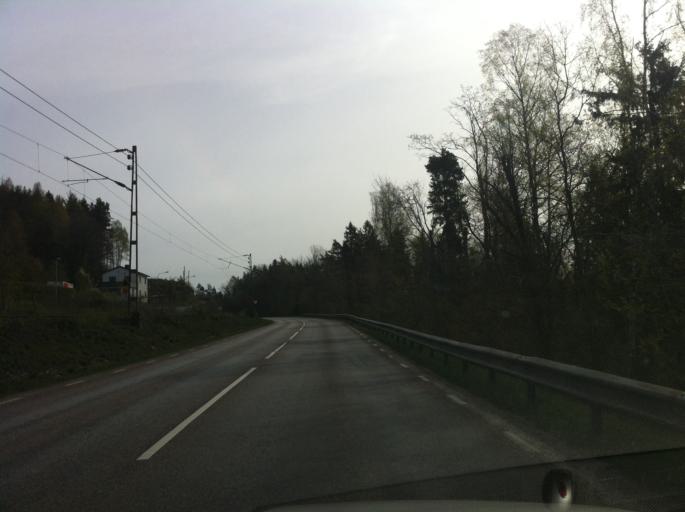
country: SE
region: Vaestra Goetaland
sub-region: Bollebygds Kommun
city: Bollebygd
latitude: 57.6681
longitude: 12.5790
